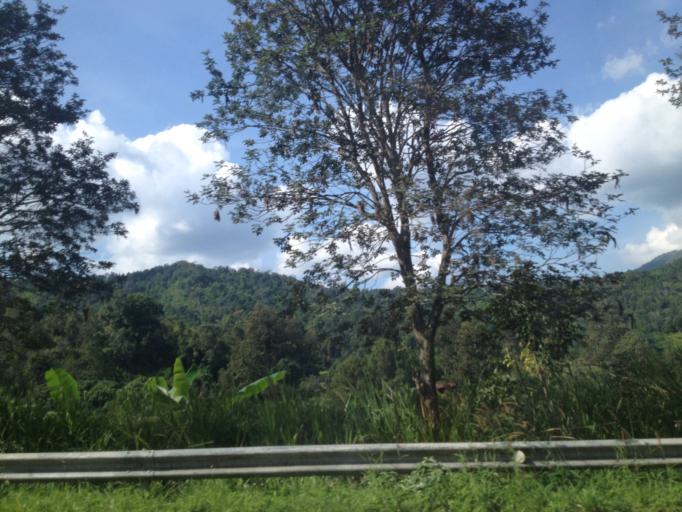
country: TH
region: Chiang Mai
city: Samoeng
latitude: 18.8109
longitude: 98.8161
